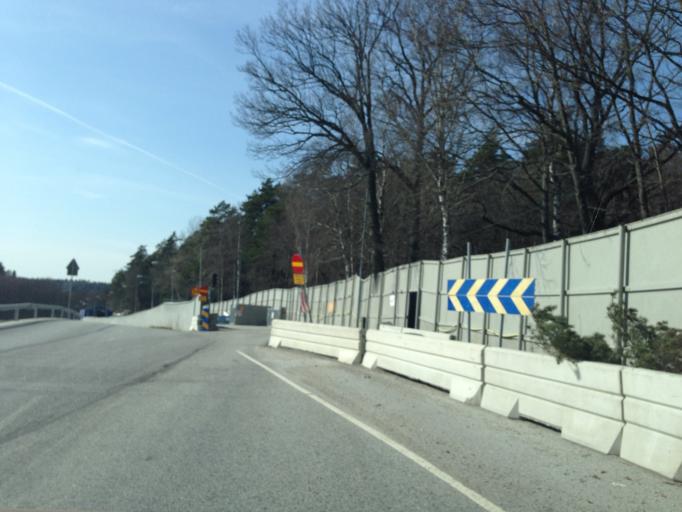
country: SE
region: Stockholm
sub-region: Botkyrka Kommun
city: Eriksberg
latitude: 59.2402
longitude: 17.8071
